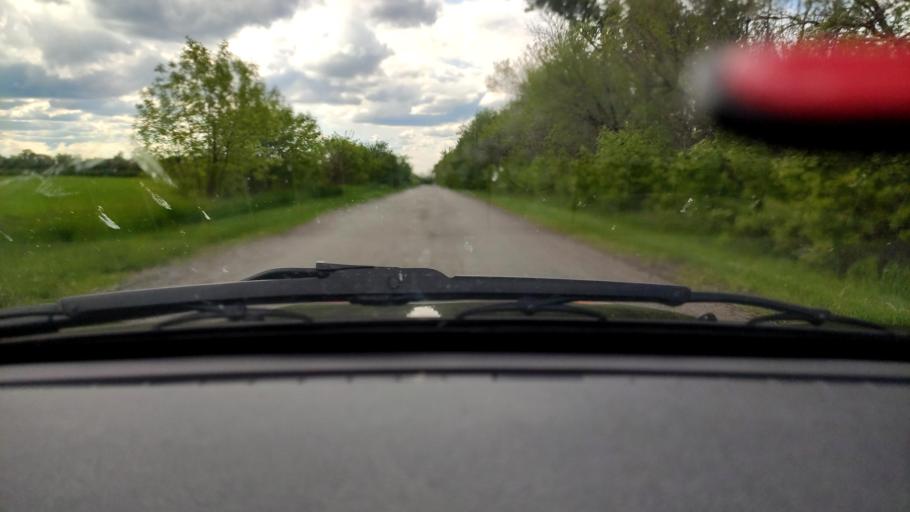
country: RU
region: Voronezj
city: Uryv-Pokrovka
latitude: 51.1445
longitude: 39.0667
